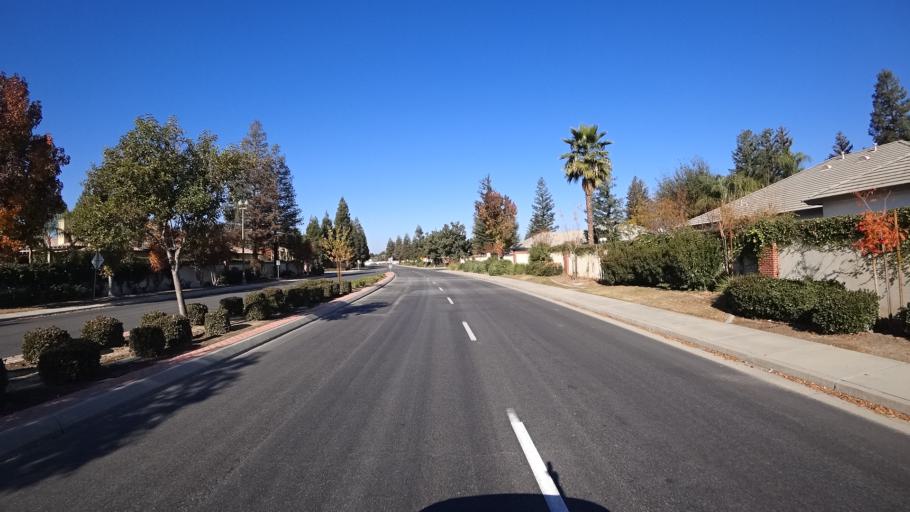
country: US
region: California
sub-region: Kern County
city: Greenacres
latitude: 35.3262
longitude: -119.1186
